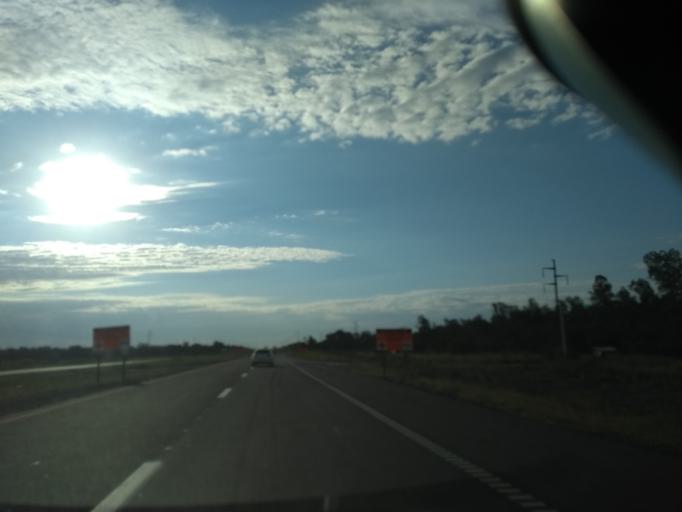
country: AR
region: Chaco
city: Puerto Tirol
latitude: -27.2733
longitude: -59.1410
